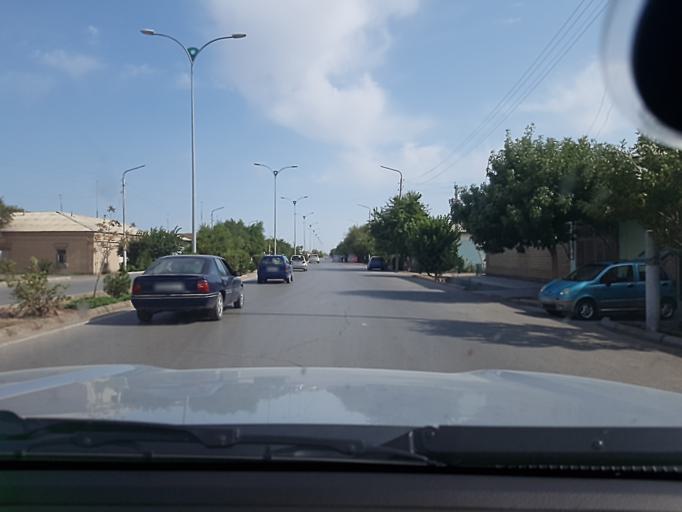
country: TM
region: Dasoguz
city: Dasoguz
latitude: 41.8351
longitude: 59.9812
